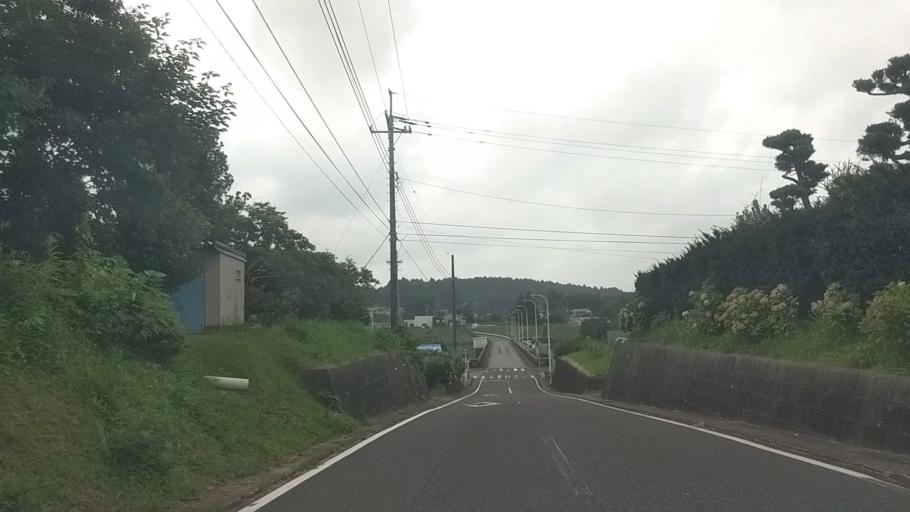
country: JP
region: Chiba
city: Kawaguchi
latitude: 35.2293
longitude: 140.0874
